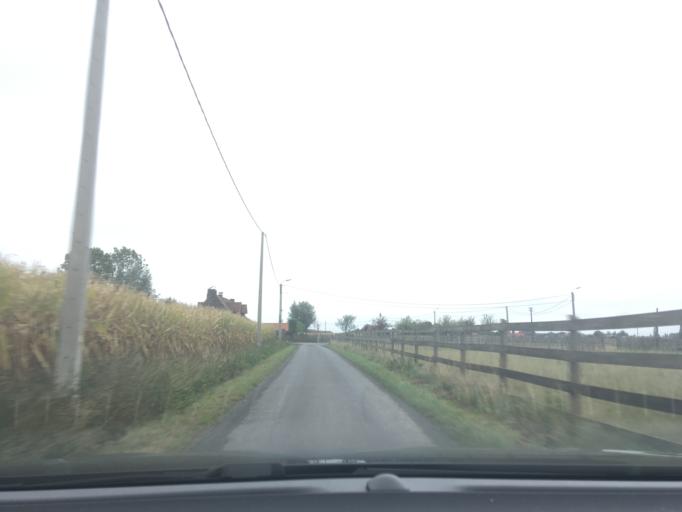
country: BE
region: Flanders
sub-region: Provincie West-Vlaanderen
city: Ledegem
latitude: 50.8821
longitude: 3.1318
